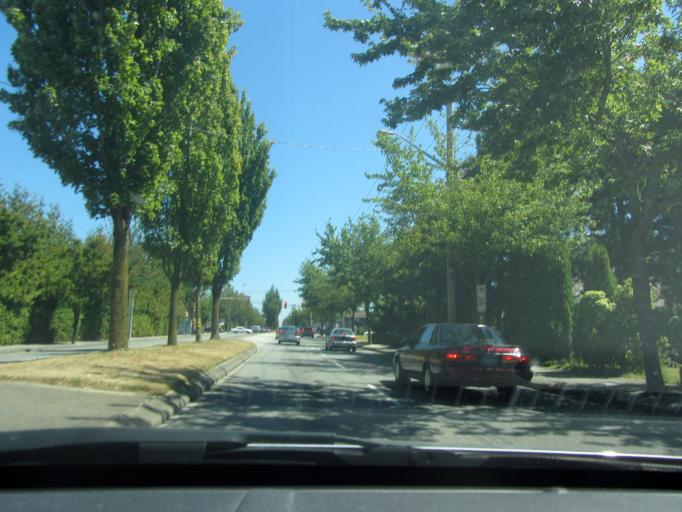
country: CA
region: British Columbia
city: Delta
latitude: 49.1339
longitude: -122.8808
